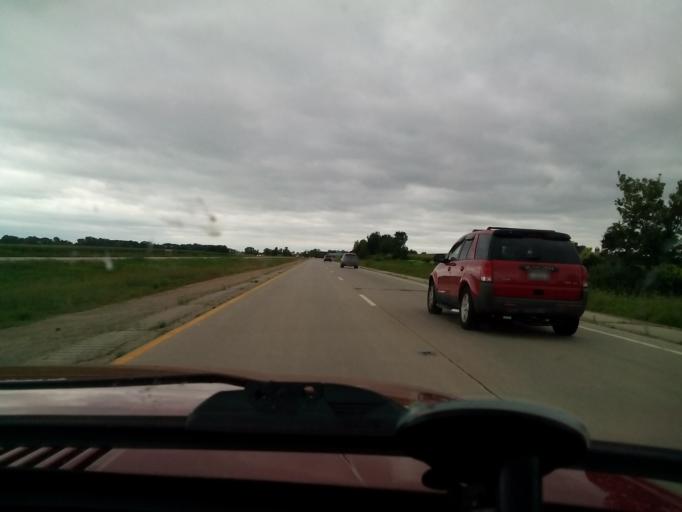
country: US
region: Wisconsin
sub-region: Columbia County
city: Columbus
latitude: 43.2842
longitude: -89.0801
